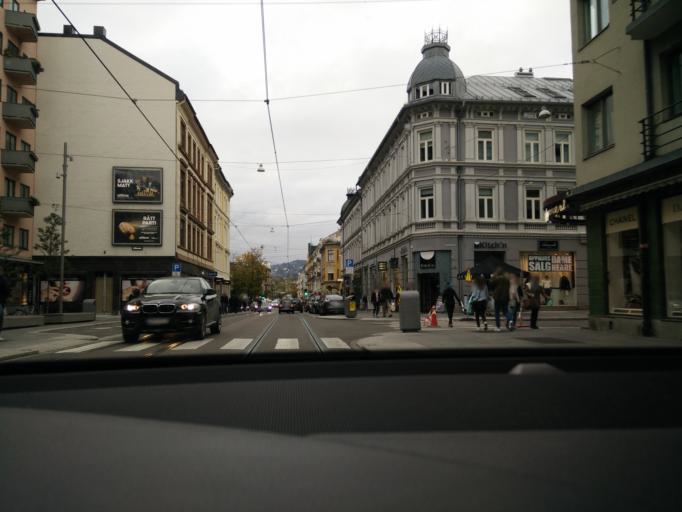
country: NO
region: Oslo
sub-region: Oslo
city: Oslo
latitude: 59.9272
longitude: 10.7203
